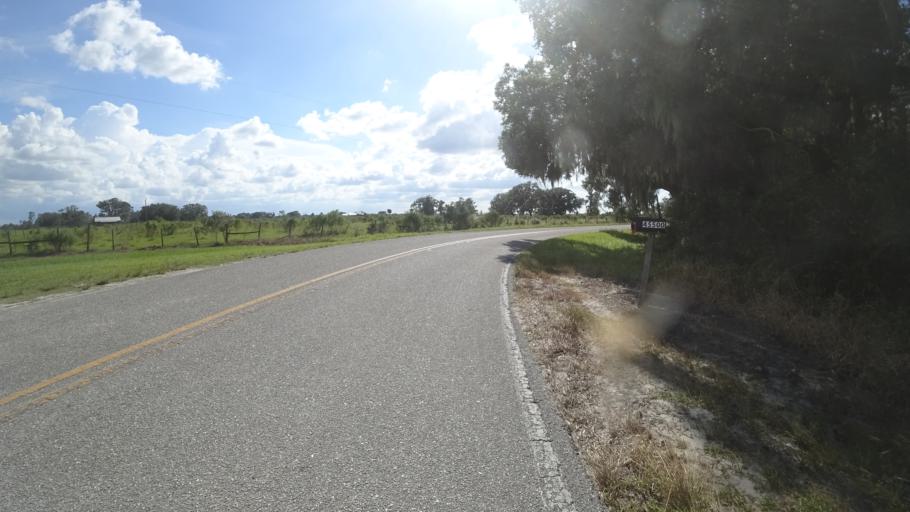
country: US
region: Florida
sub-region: DeSoto County
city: Nocatee
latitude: 27.2722
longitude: -82.0767
